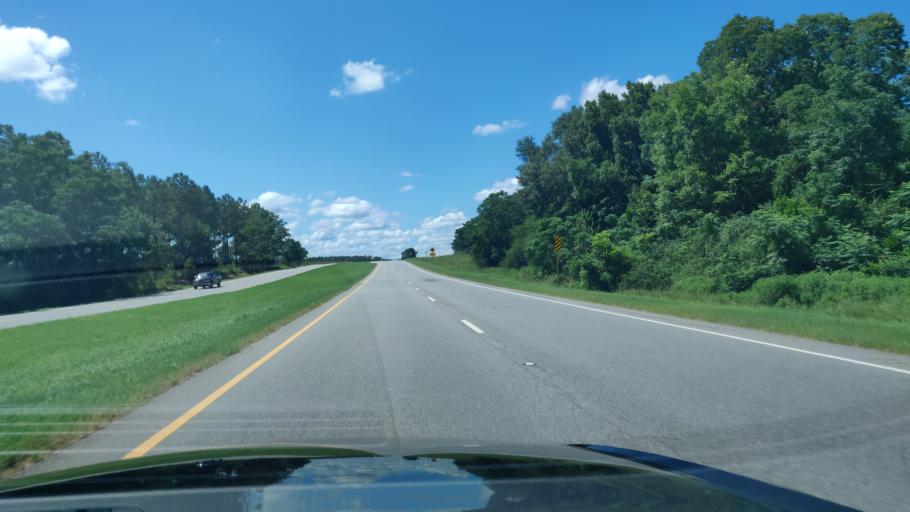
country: US
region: Georgia
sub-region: Terrell County
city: Dawson
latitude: 31.8525
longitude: -84.4762
